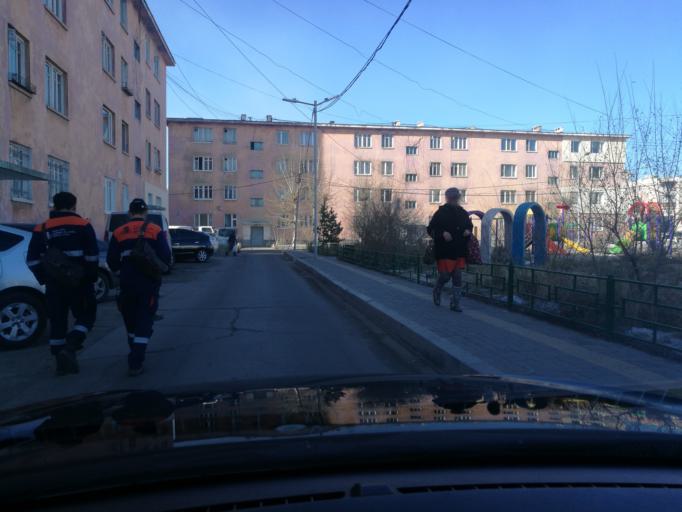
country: MN
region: Ulaanbaatar
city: Ulaanbaatar
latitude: 47.8998
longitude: 106.9052
